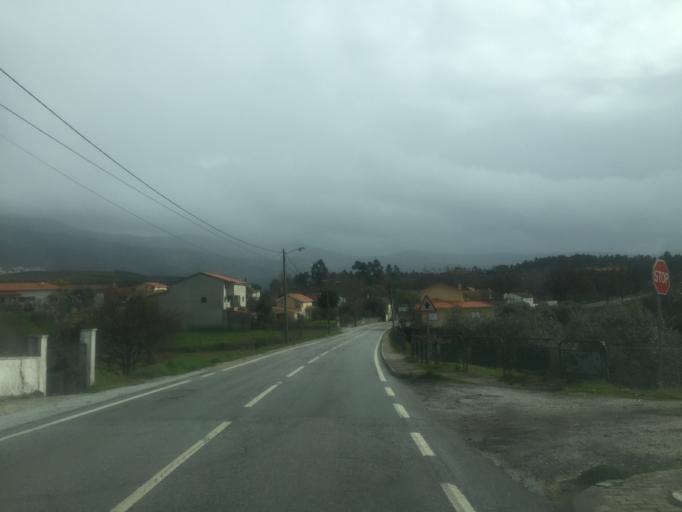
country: PT
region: Guarda
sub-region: Seia
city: Seia
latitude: 40.4001
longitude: -7.7417
